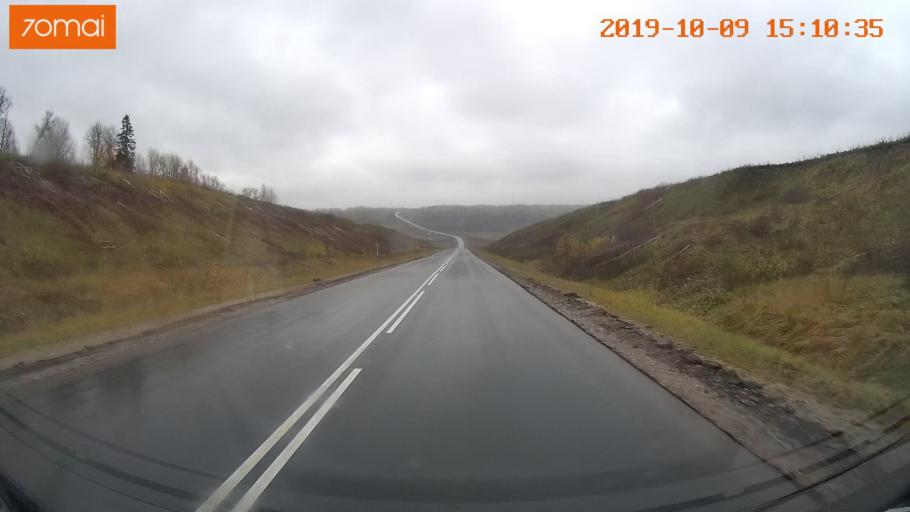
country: RU
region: Kostroma
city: Susanino
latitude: 58.1763
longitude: 41.6385
